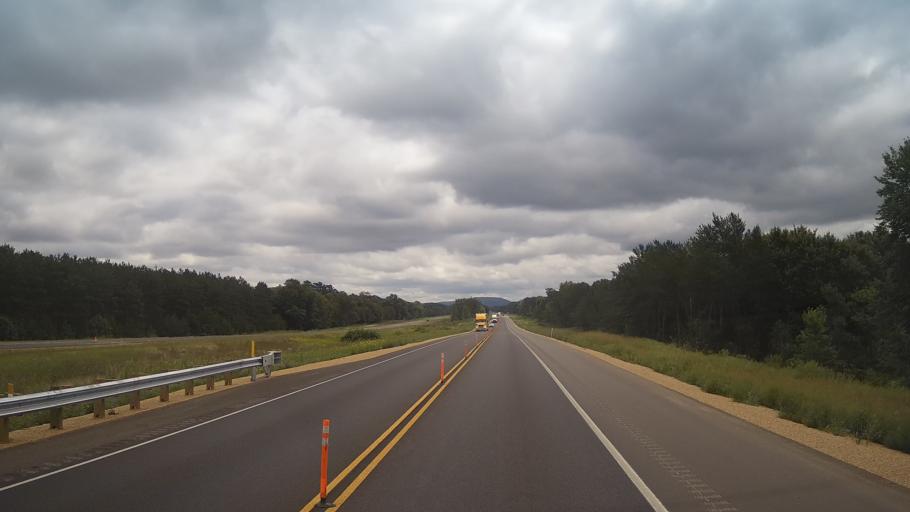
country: US
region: Wisconsin
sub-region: Monroe County
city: Sparta
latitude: 43.9434
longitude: -90.7290
